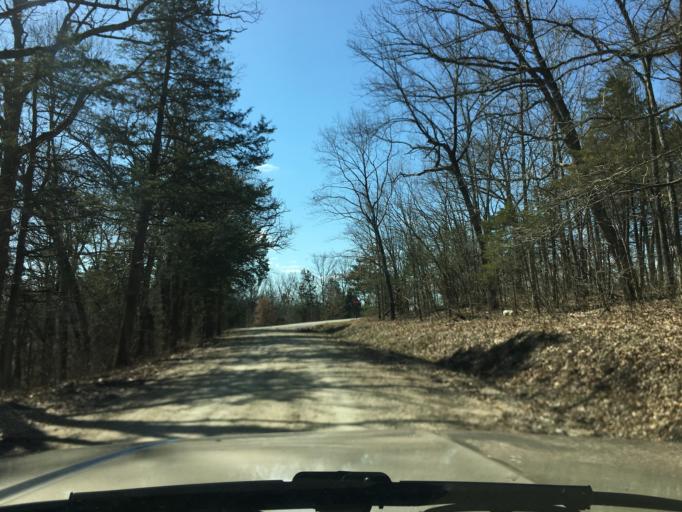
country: US
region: Missouri
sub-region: Franklin County
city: Gerald
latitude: 38.5180
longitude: -91.3210
